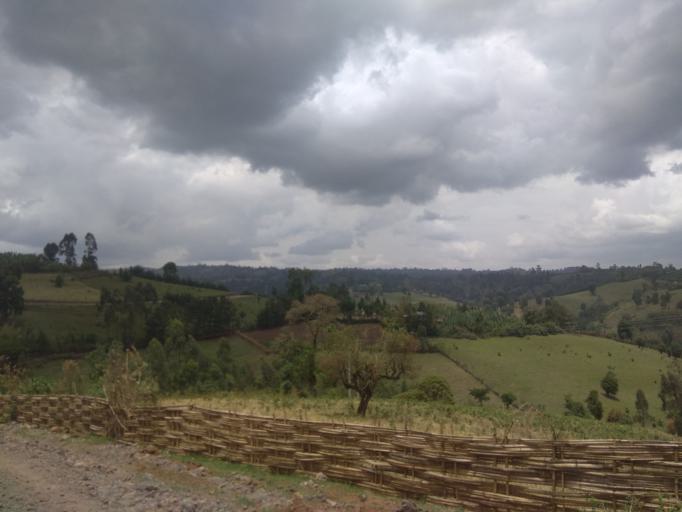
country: ET
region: Oromiya
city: Guder
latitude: 8.7497
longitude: 37.6295
